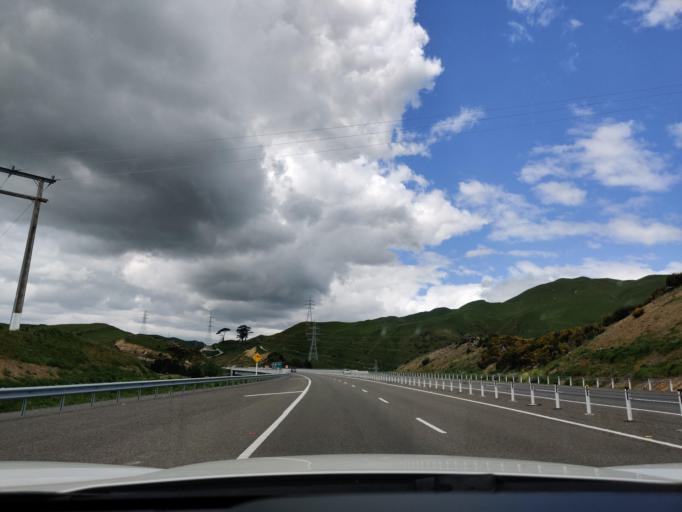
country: NZ
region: Wellington
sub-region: Porirua City
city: Porirua
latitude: -41.1556
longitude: 174.8713
